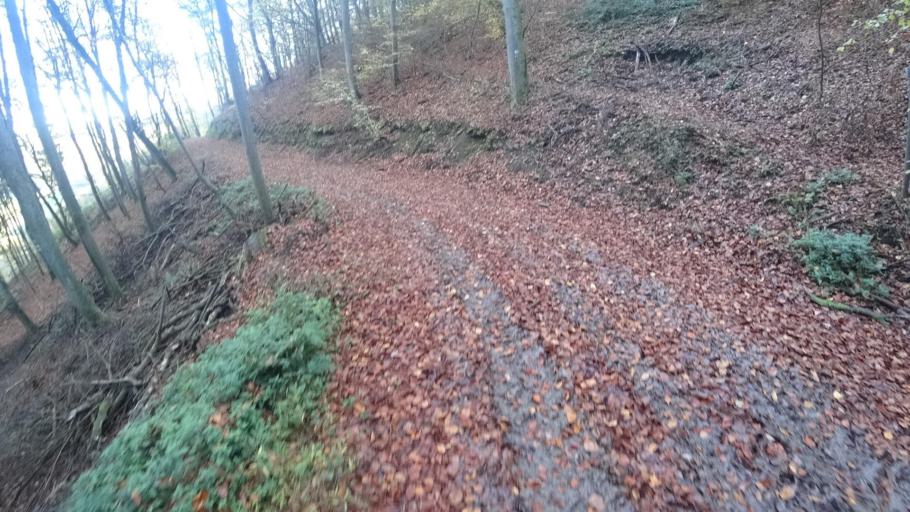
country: DE
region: Rheinland-Pfalz
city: Lind
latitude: 50.5065
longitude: 6.9138
